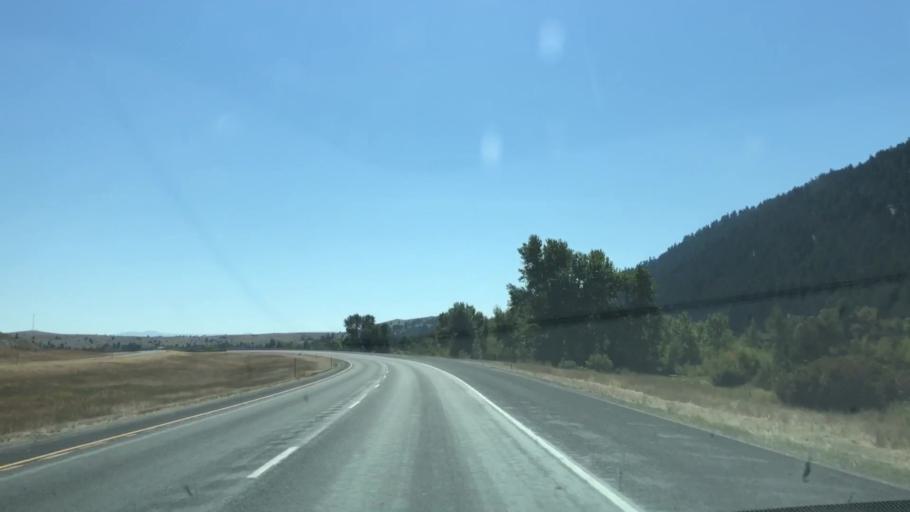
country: US
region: Montana
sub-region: Powell County
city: Deer Lodge
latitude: 46.5453
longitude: -112.8526
